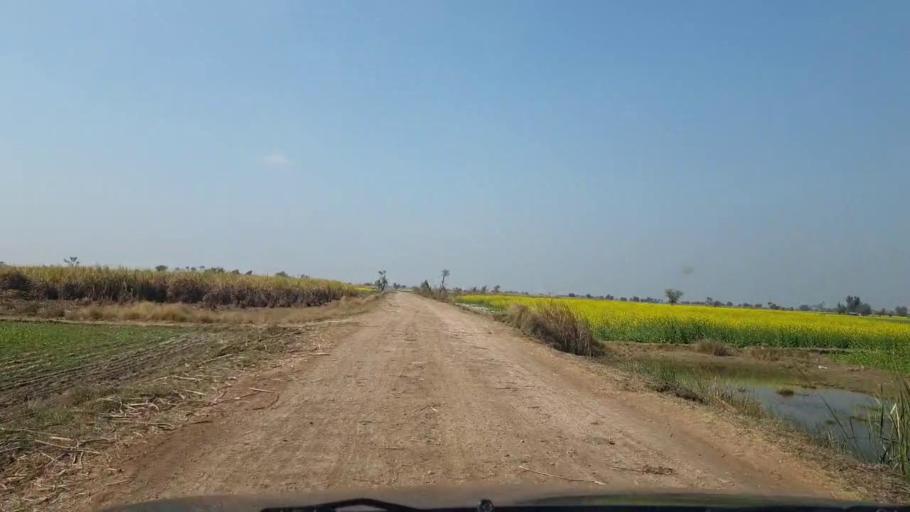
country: PK
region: Sindh
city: Sinjhoro
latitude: 26.0459
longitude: 68.7467
